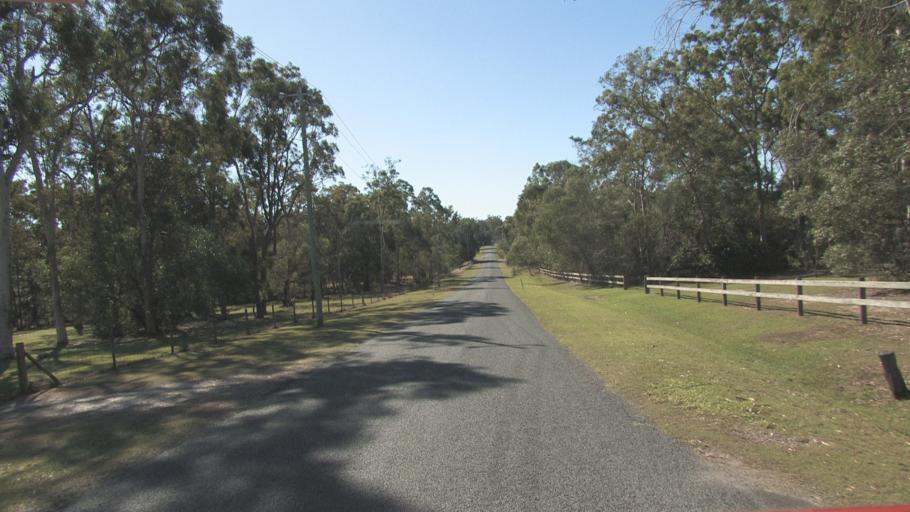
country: AU
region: Queensland
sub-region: Logan
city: Chambers Flat
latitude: -27.7373
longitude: 153.0709
